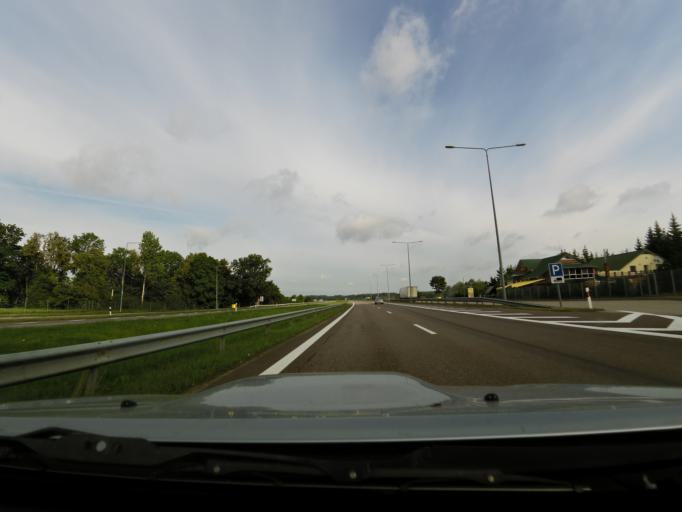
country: LT
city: Sirvintos
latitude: 55.0755
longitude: 24.8805
